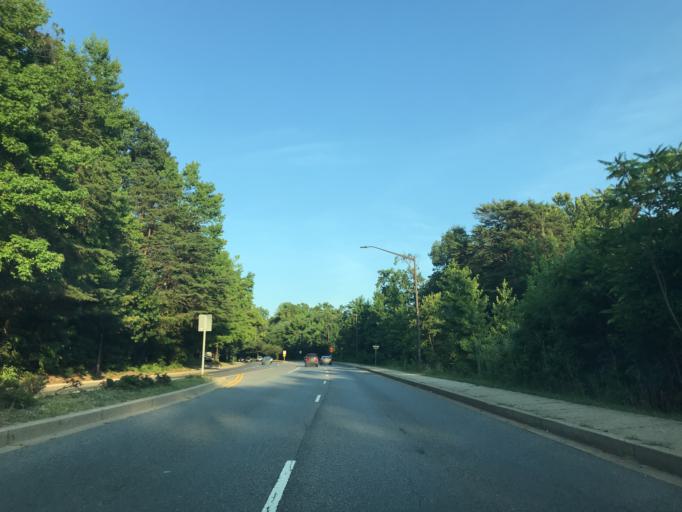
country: US
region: Maryland
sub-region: Anne Arundel County
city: Robinwood
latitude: 38.9529
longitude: -76.5013
